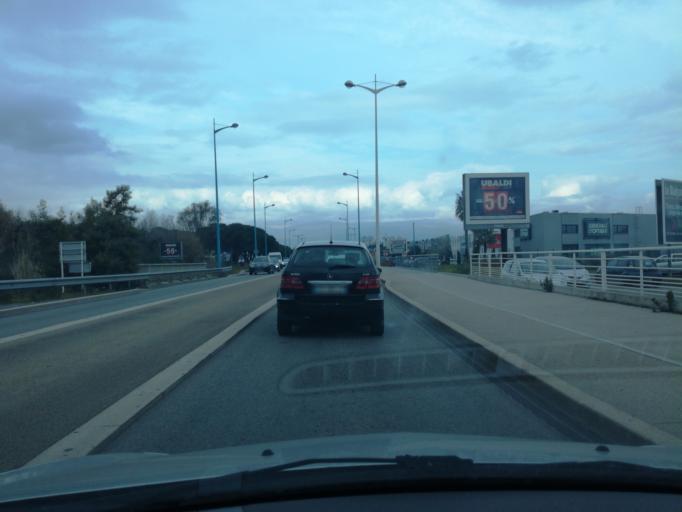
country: FR
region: Provence-Alpes-Cote d'Azur
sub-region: Departement des Alpes-Maritimes
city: Mandelieu-la-Napoule
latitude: 43.5524
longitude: 6.9553
